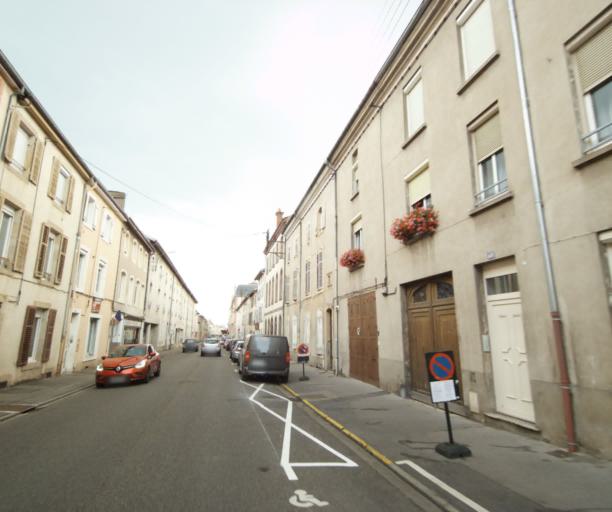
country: FR
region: Lorraine
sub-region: Departement de Meurthe-et-Moselle
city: Luneville
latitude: 48.5891
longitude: 6.4895
